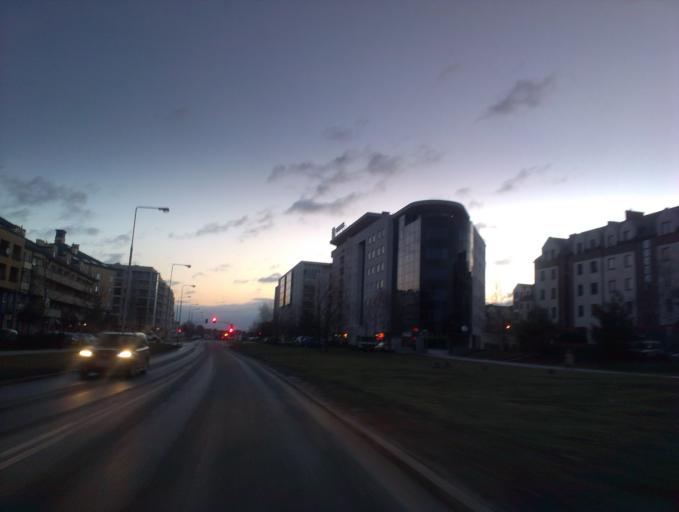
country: PL
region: Masovian Voivodeship
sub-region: Warszawa
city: Kabaty
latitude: 52.1313
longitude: 21.0689
